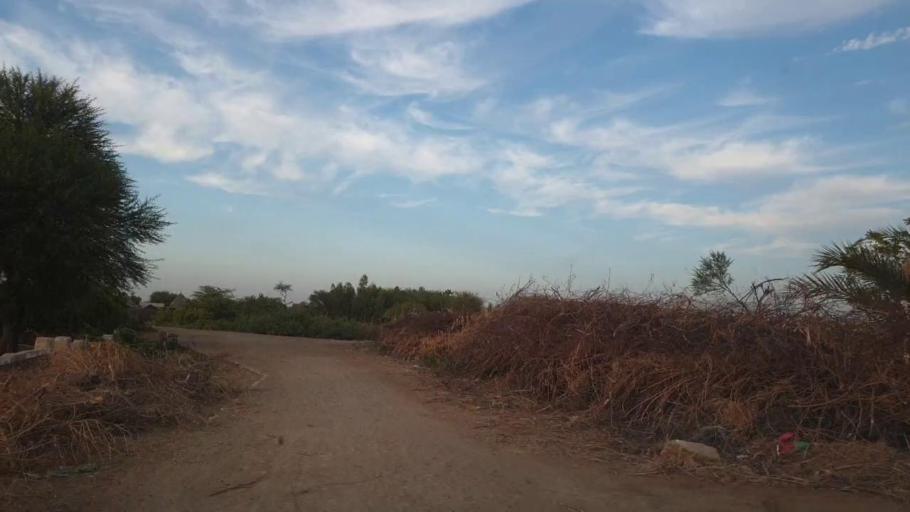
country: PK
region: Sindh
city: Pithoro
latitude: 25.6032
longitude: 69.2039
